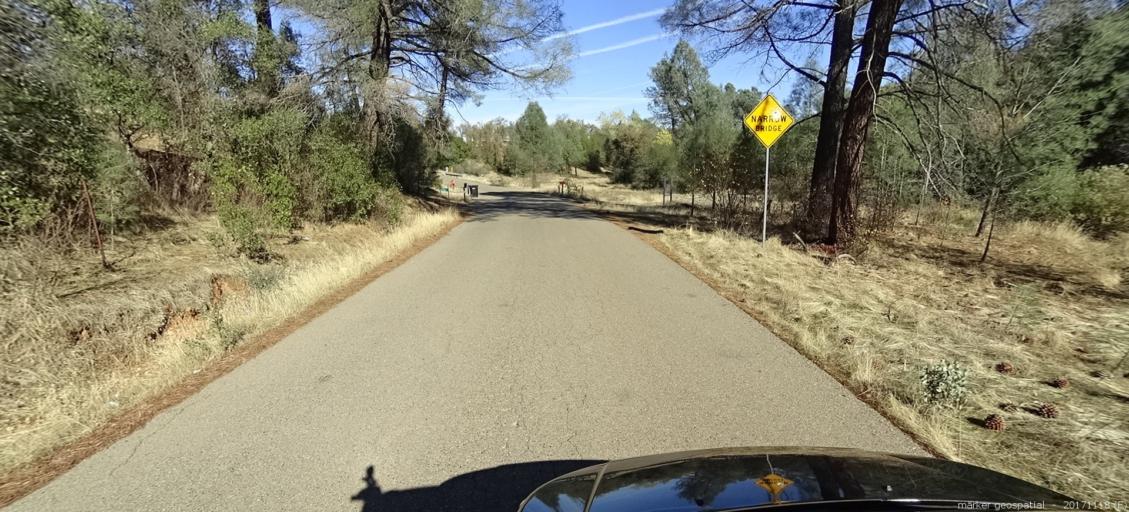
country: US
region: California
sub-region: Shasta County
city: Anderson
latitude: 40.4405
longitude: -122.3666
